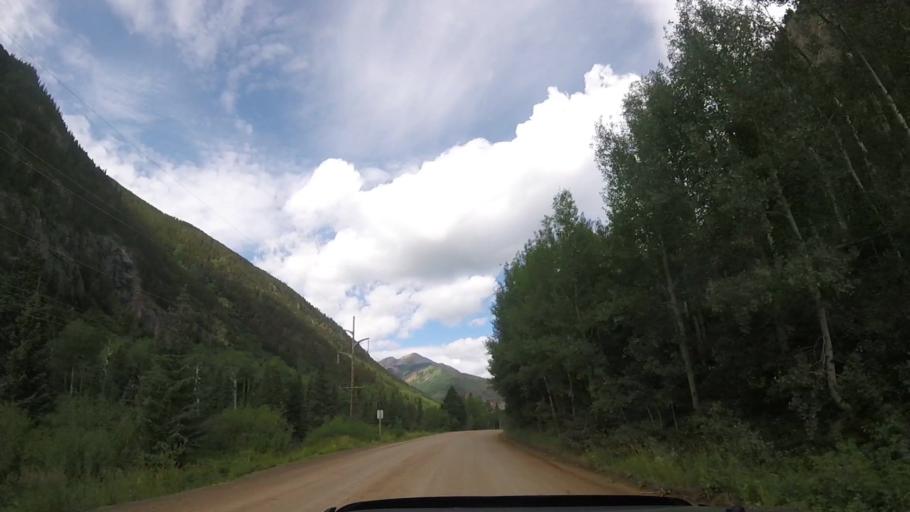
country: US
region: Colorado
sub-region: San Miguel County
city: Mountain Village
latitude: 37.8586
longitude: -107.8630
